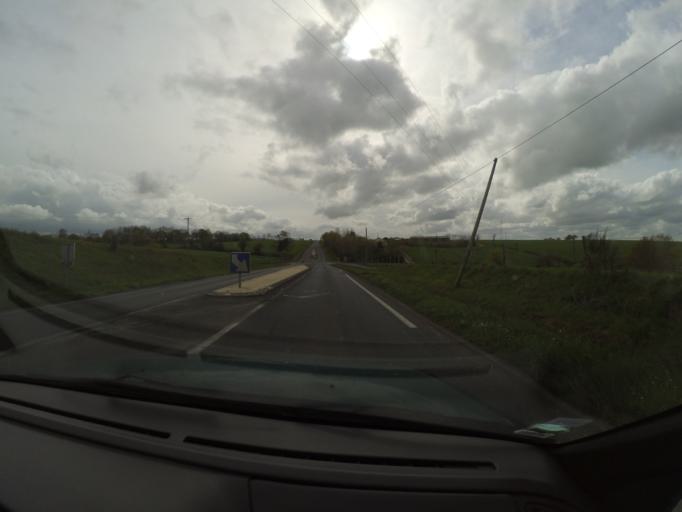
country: FR
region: Pays de la Loire
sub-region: Departement de Maine-et-Loire
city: Saint-Laurent-des-Autels
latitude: 47.2931
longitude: -1.1776
